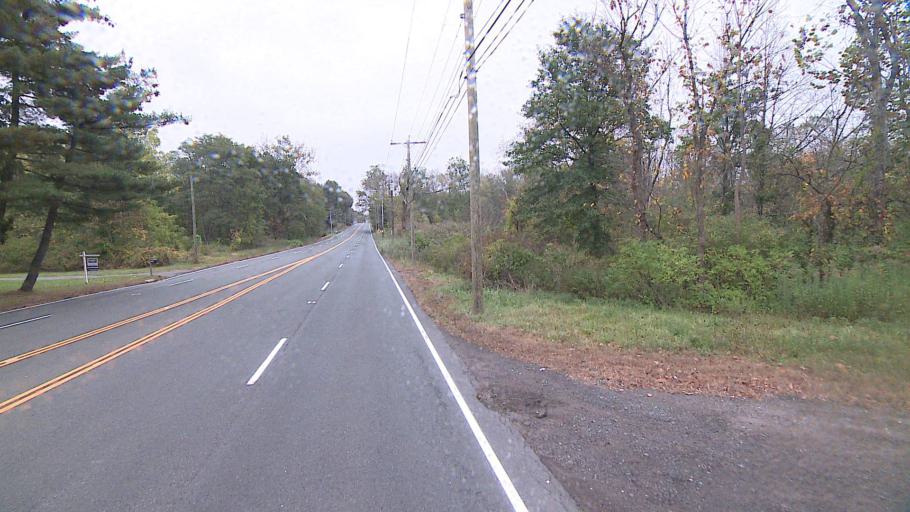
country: US
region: Connecticut
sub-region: Hartford County
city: West Hartford
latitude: 41.7871
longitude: -72.7643
